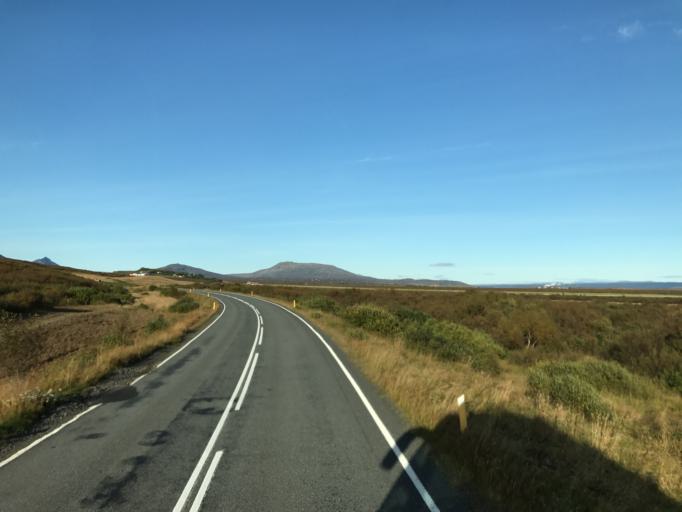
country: IS
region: South
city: Selfoss
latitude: 64.2260
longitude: -20.5727
